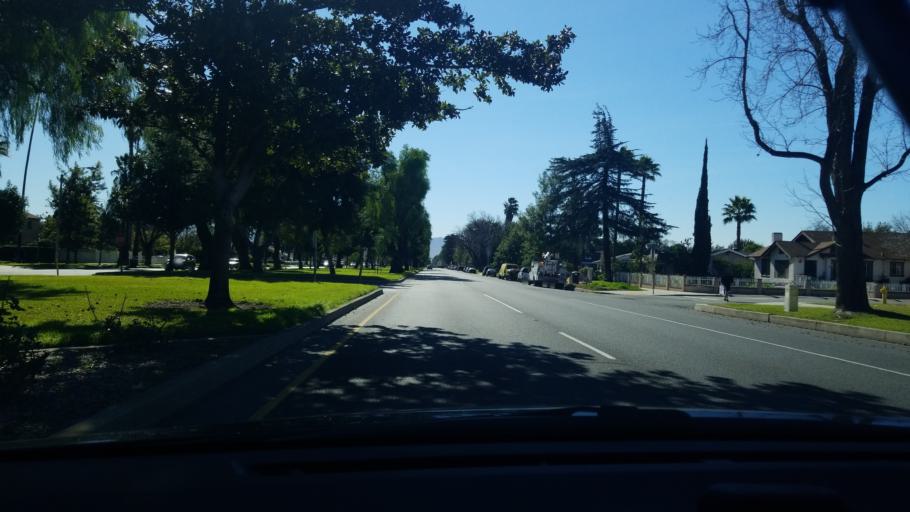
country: US
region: California
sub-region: San Bernardino County
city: Ontario
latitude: 34.0469
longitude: -117.6511
